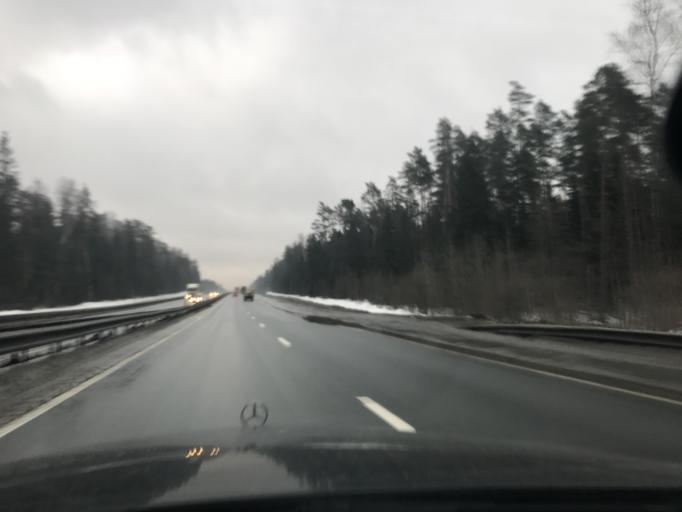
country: RU
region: Vladimir
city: Melekhovo
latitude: 56.2141
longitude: 41.3662
